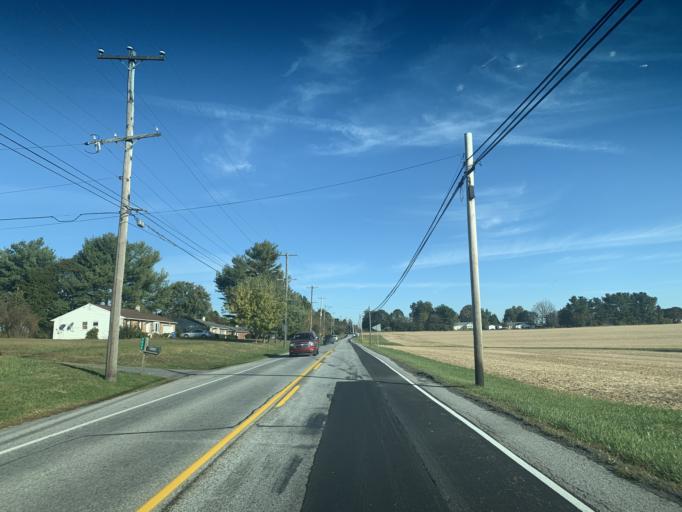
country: US
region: Pennsylvania
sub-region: Chester County
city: Parkesburg
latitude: 39.8839
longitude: -75.9223
